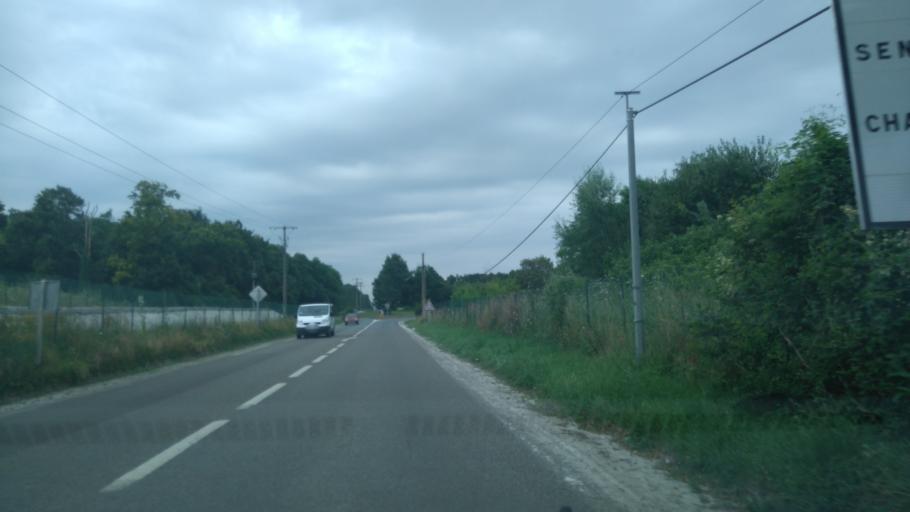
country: FR
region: Picardie
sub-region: Departement de l'Oise
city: Saint-Maximin
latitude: 49.2122
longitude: 2.4460
